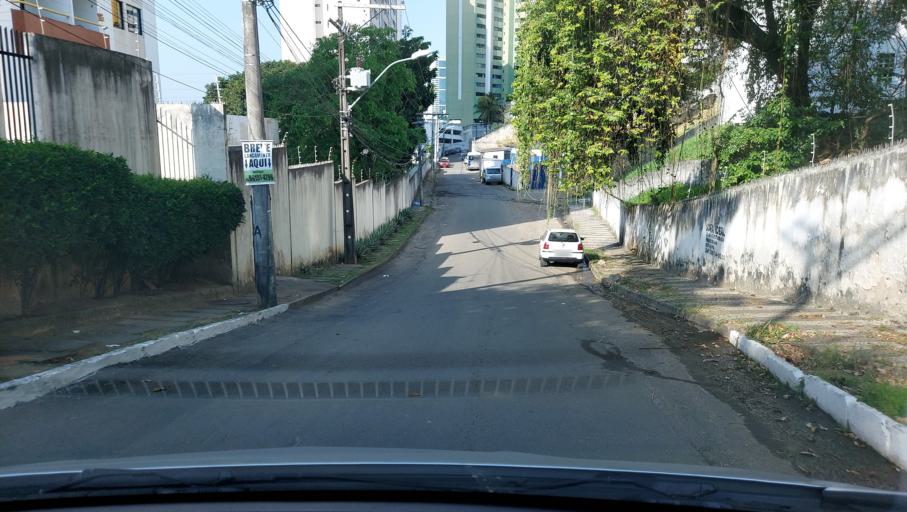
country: BR
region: Bahia
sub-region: Salvador
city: Salvador
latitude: -12.9859
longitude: -38.4699
